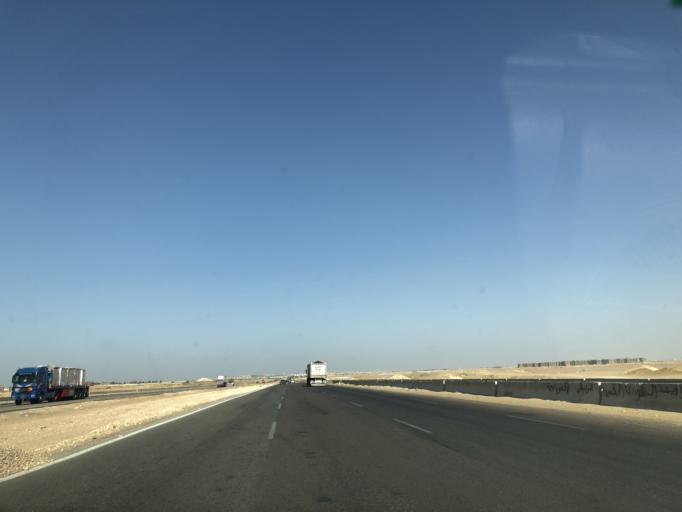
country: EG
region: Muhafazat al Minufiyah
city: Ashmun
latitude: 30.0677
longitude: 30.8697
